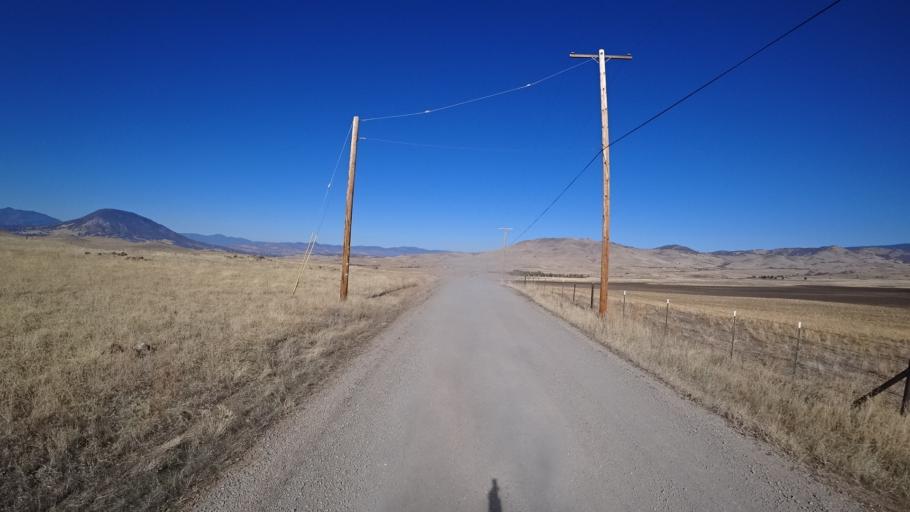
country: US
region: California
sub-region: Siskiyou County
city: Montague
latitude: 41.8005
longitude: -122.4161
